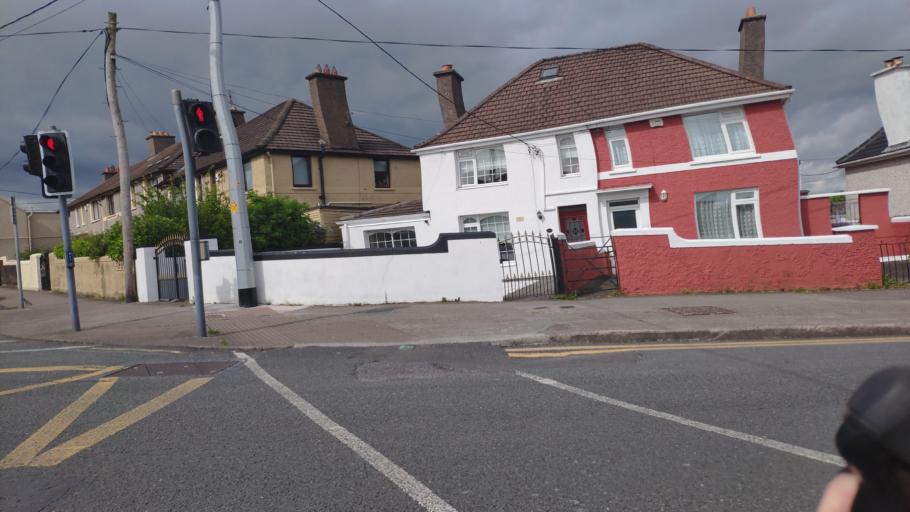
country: IE
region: Munster
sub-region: County Cork
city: Cork
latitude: 51.9047
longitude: -8.4793
